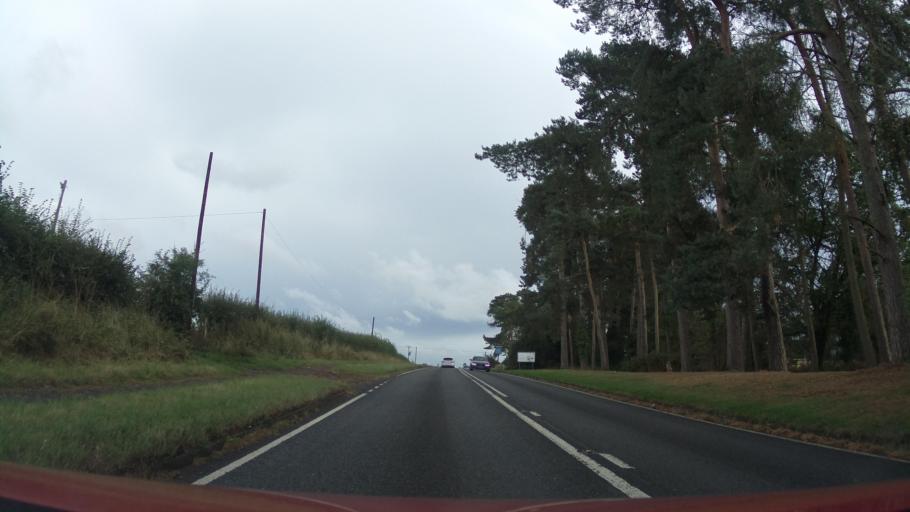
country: GB
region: England
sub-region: Worcestershire
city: Kidderminster
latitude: 52.3694
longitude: -2.1995
